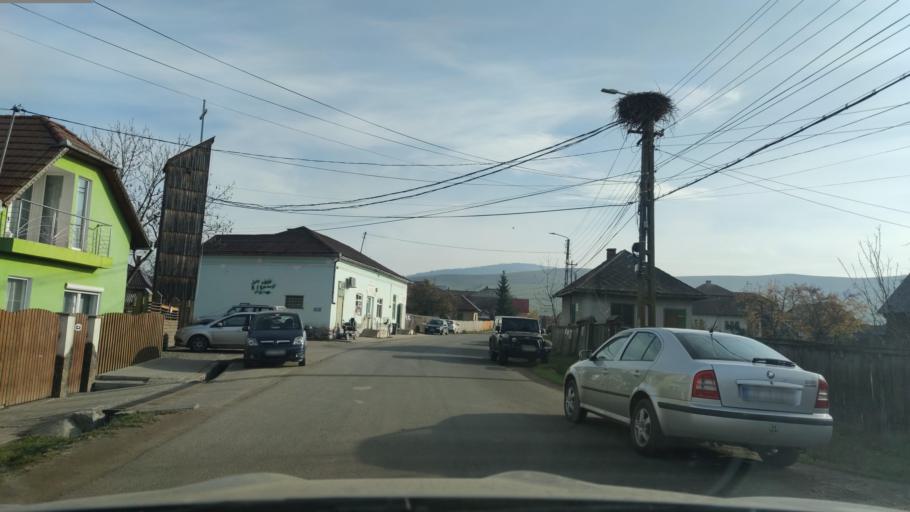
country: RO
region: Harghita
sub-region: Comuna Ditrau
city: Ditrau
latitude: 46.8091
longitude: 25.5096
